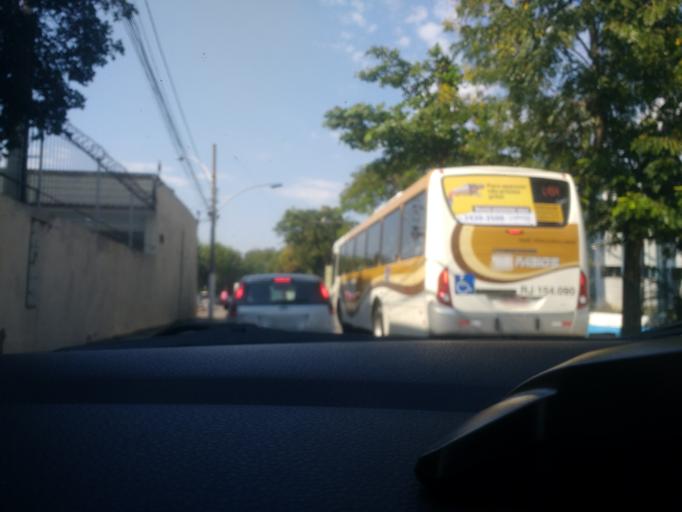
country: BR
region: Rio de Janeiro
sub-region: Duque De Caxias
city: Duque de Caxias
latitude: -22.8004
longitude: -43.2933
